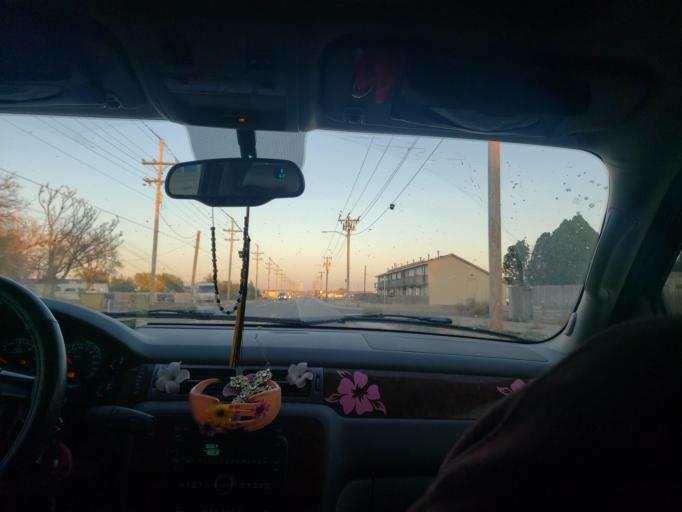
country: US
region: Kansas
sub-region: Finney County
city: Garden City
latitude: 37.9895
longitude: -100.8894
